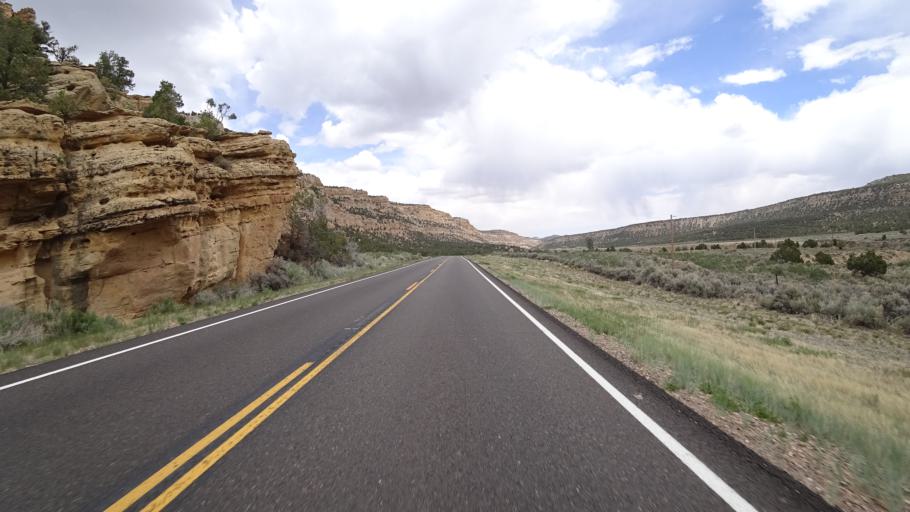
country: US
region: Utah
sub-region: Garfield County
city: Panguitch
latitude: 37.7253
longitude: -111.7758
